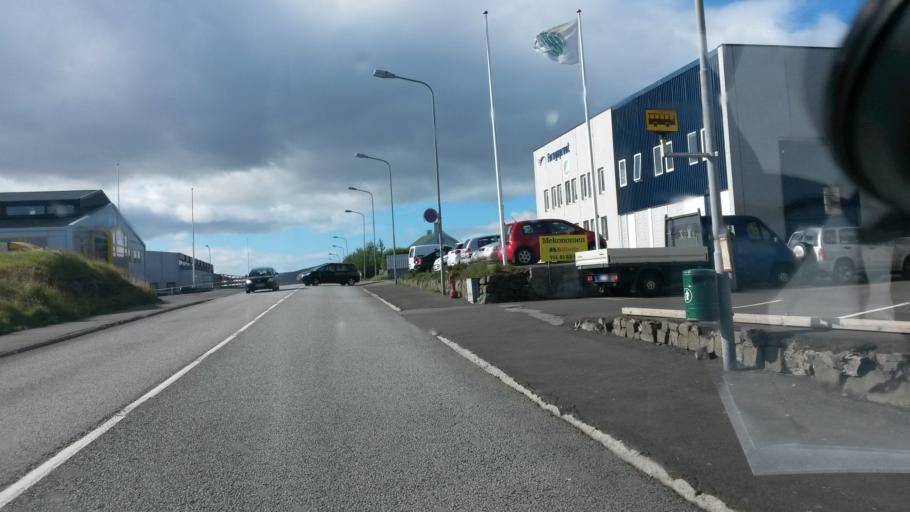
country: FO
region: Streymoy
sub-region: Torshavn
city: Torshavn
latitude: 62.0212
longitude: -6.7650
